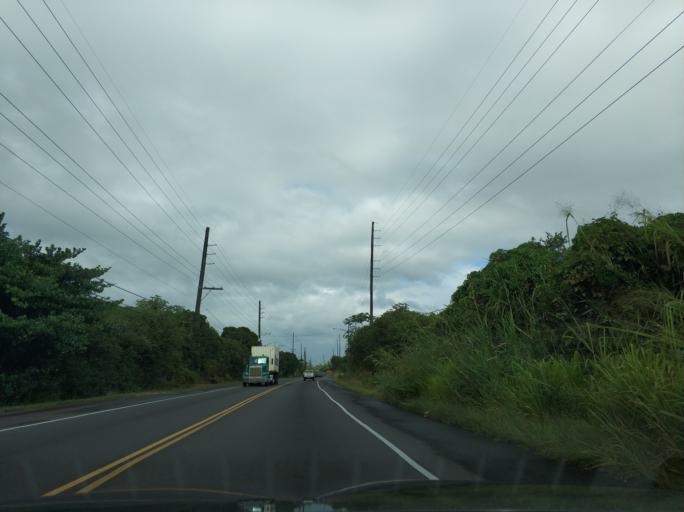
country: US
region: Hawaii
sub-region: Hawaii County
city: Orchidlands Estates
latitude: 19.5736
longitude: -155.0022
